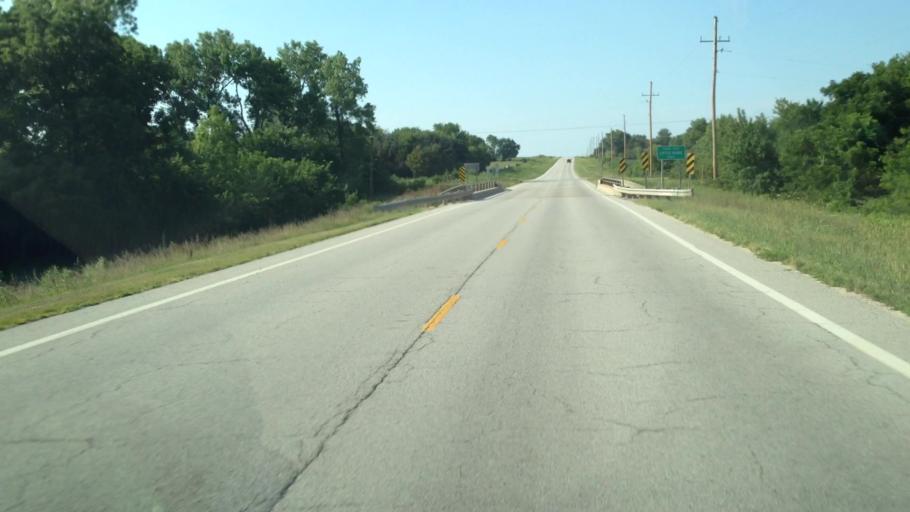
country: US
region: Kansas
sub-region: Allen County
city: Iola
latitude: 37.9933
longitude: -95.1705
